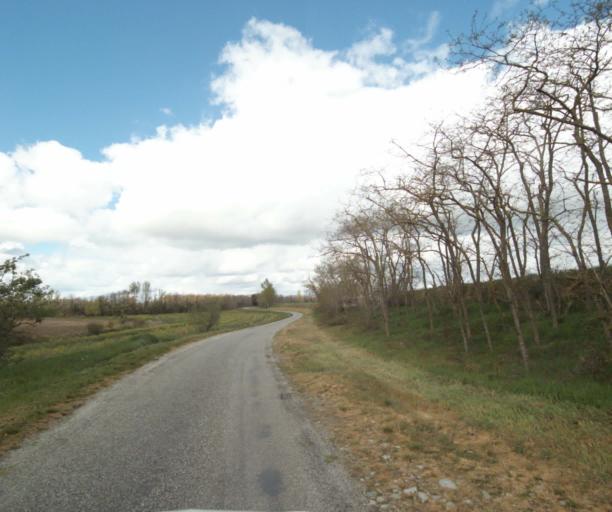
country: FR
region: Midi-Pyrenees
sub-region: Departement de l'Ariege
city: Saverdun
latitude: 43.2656
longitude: 1.5839
